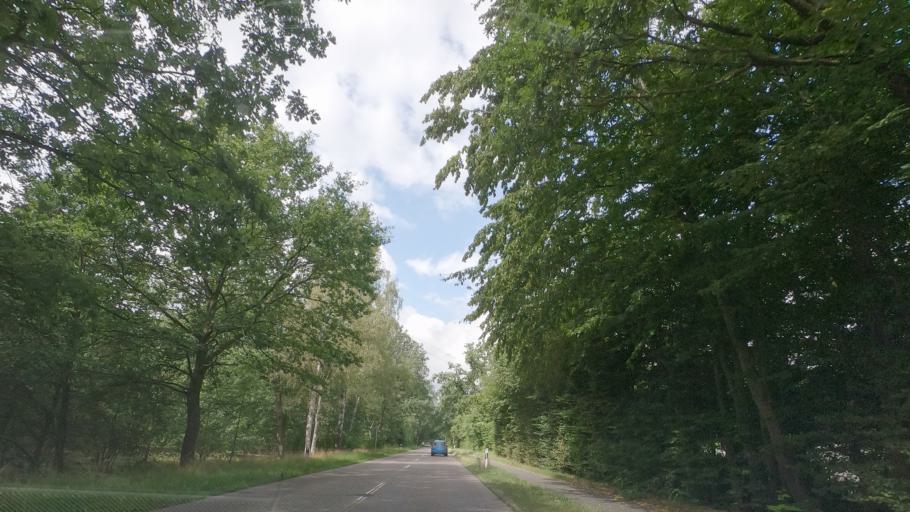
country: DE
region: Lower Saxony
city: Schwanewede
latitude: 53.2313
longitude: 8.5810
